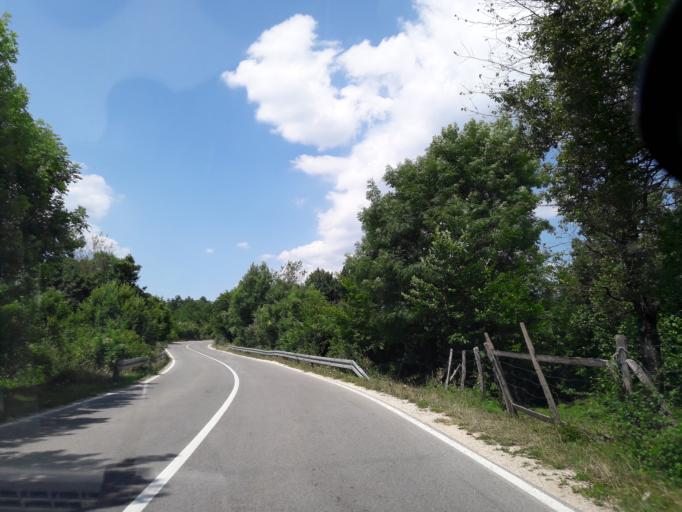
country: BA
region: Republika Srpska
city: Sipovo
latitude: 44.1715
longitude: 17.1672
